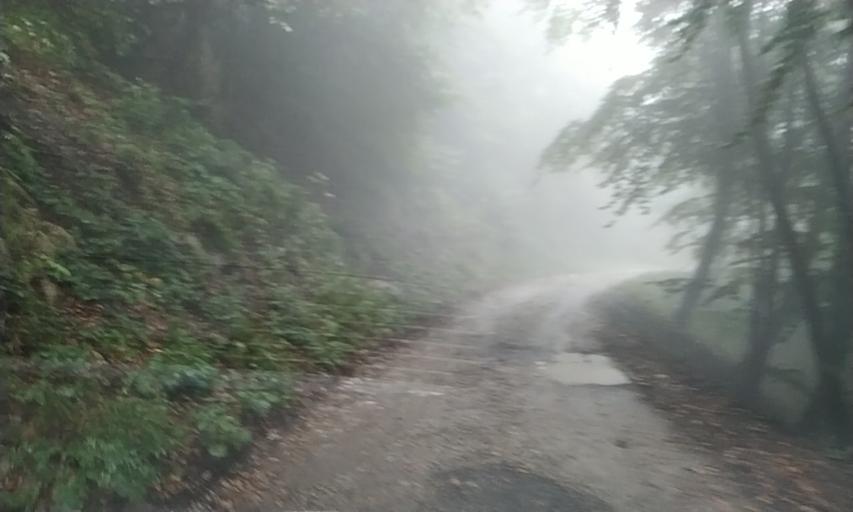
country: IT
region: Piedmont
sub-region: Provincia di Vercelli
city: Civiasco
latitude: 45.8370
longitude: 8.3208
